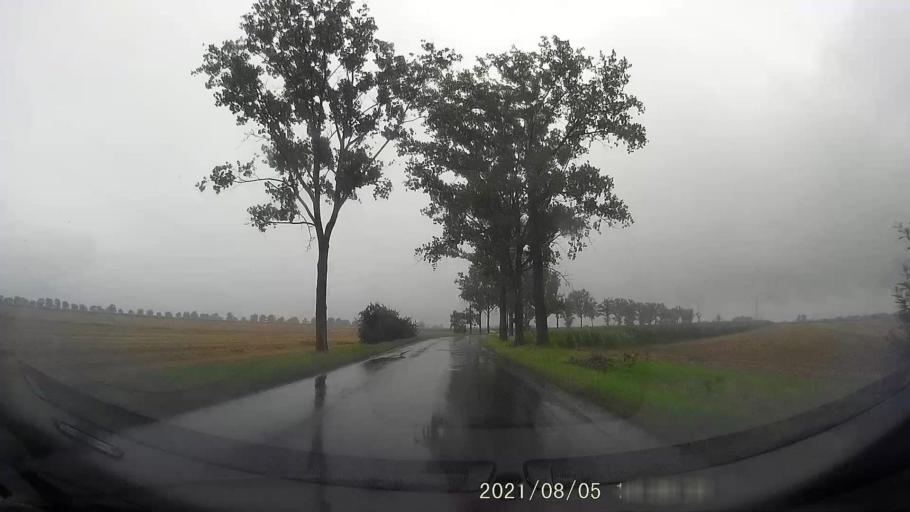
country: PL
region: Opole Voivodeship
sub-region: Powiat nyski
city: Korfantow
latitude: 50.4828
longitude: 17.6175
